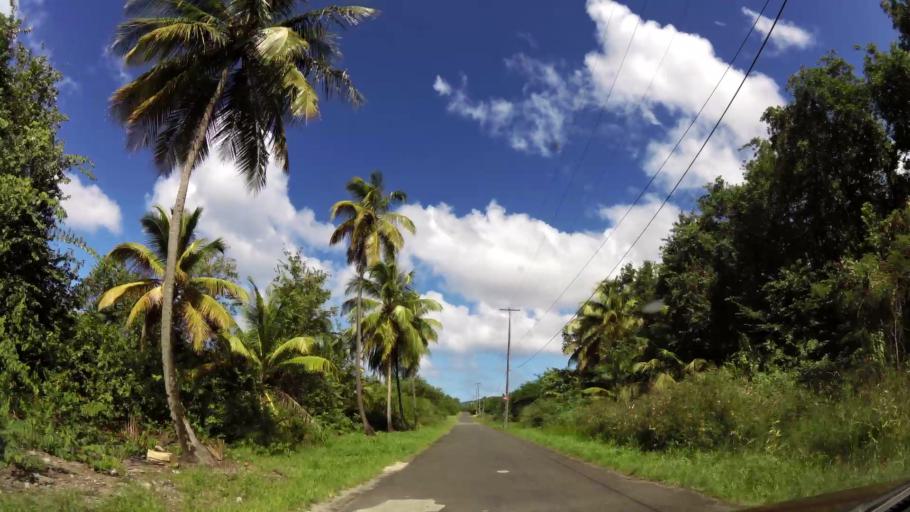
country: DM
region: Saint John
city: Portsmouth
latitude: 15.5865
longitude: -61.4641
